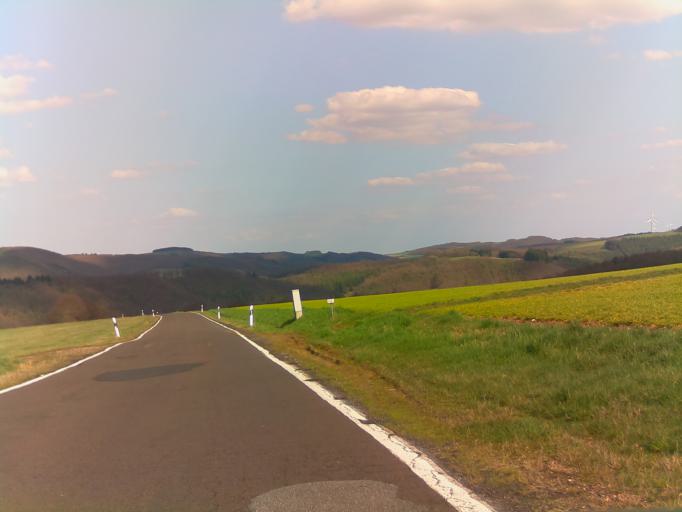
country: DE
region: Rheinland-Pfalz
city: Schmidthachenbach
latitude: 49.7367
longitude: 7.4820
